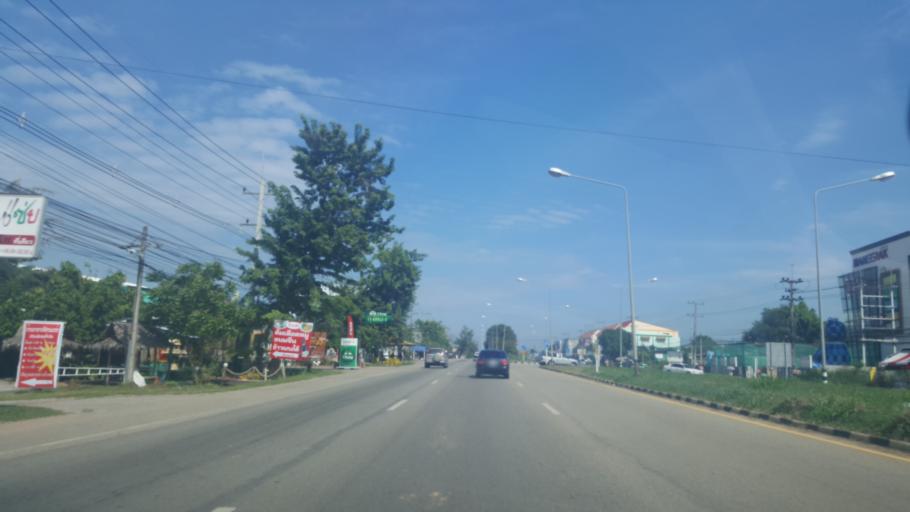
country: TH
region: Chon Buri
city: Sattahip
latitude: 12.7084
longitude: 100.8891
